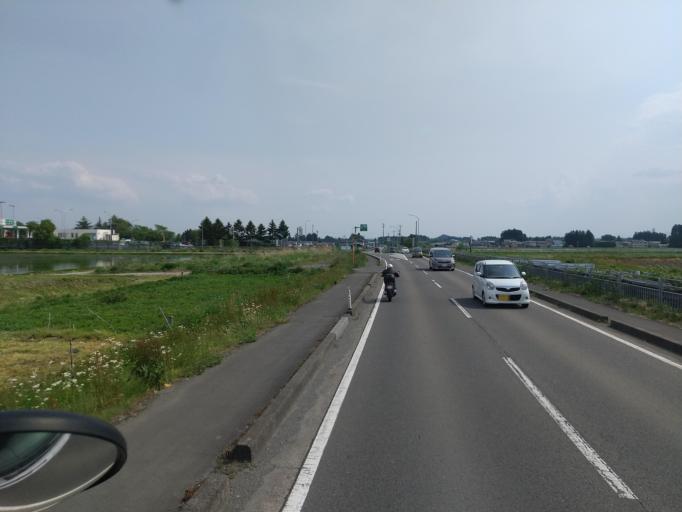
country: JP
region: Iwate
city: Hanamaki
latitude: 39.3874
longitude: 141.0872
